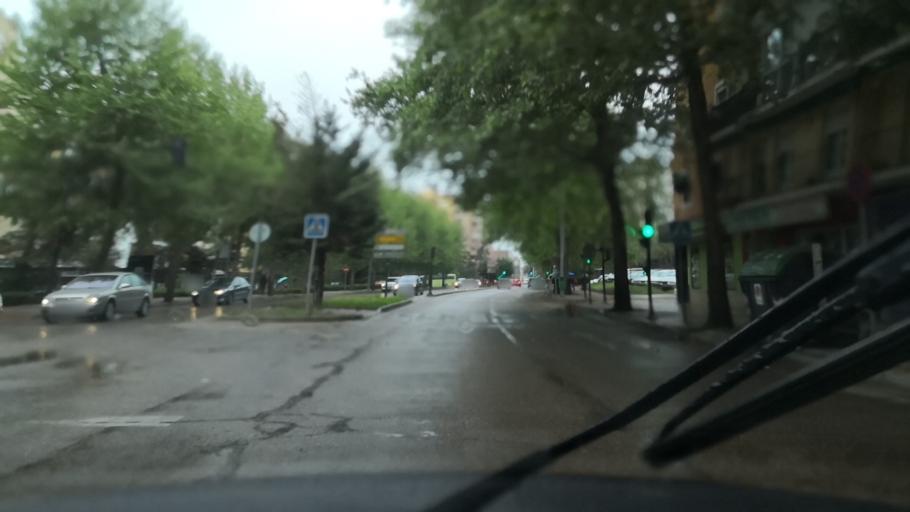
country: ES
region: Extremadura
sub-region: Provincia de Badajoz
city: Badajoz
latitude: 38.8674
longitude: -6.9731
